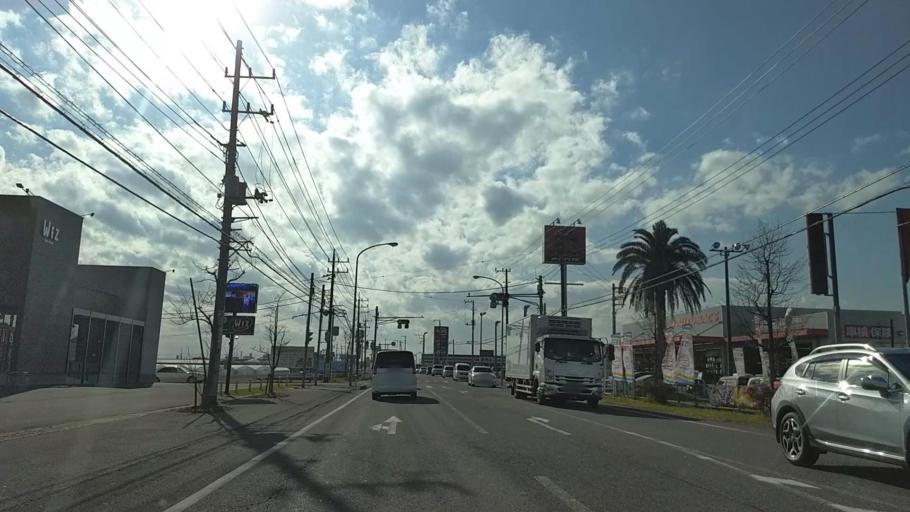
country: JP
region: Chiba
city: Togane
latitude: 35.5808
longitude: 140.3846
